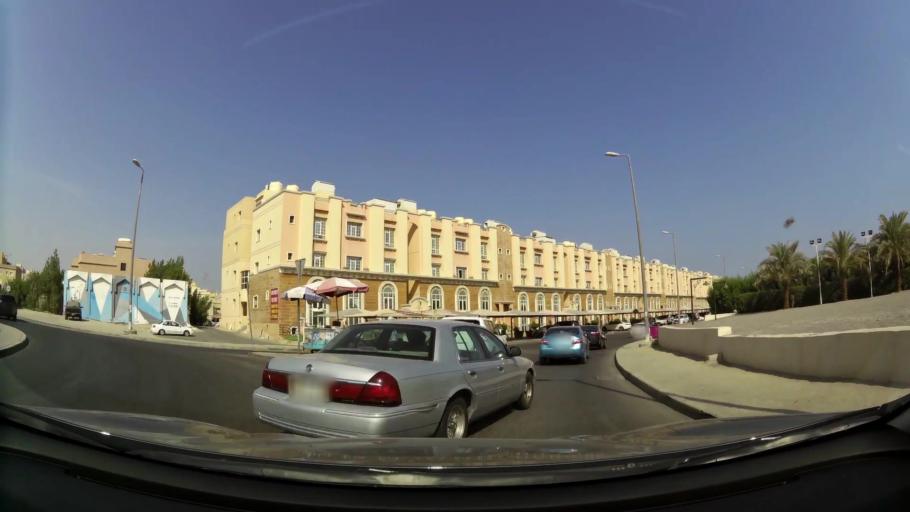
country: KW
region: Al Ahmadi
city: Al Manqaf
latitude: 29.1115
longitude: 48.1234
